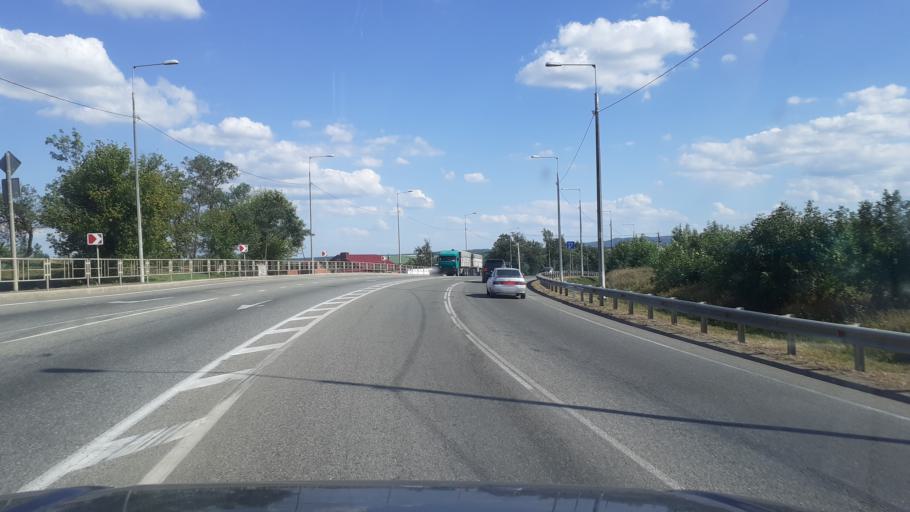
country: RU
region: Krasnodarskiy
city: Severskaya
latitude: 44.8433
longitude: 38.6570
